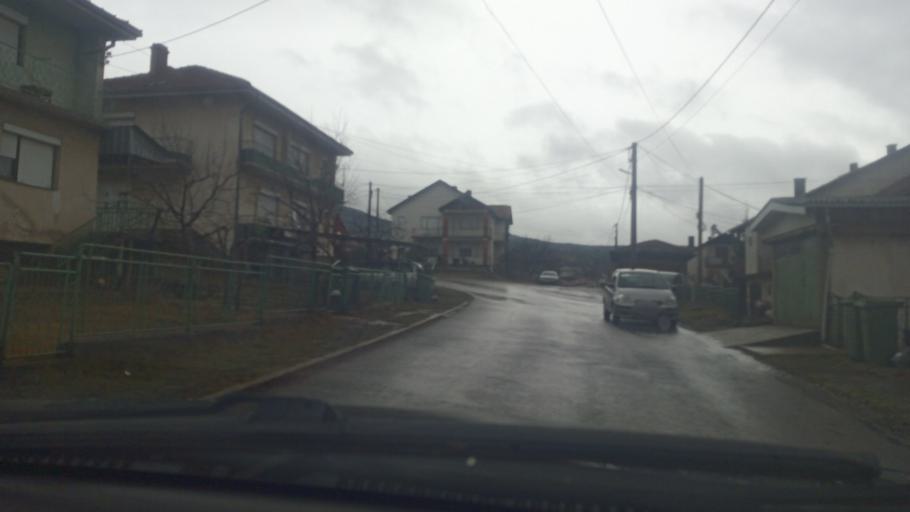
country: MK
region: Pehcevo
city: Pehcevo
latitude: 41.7645
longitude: 22.8874
